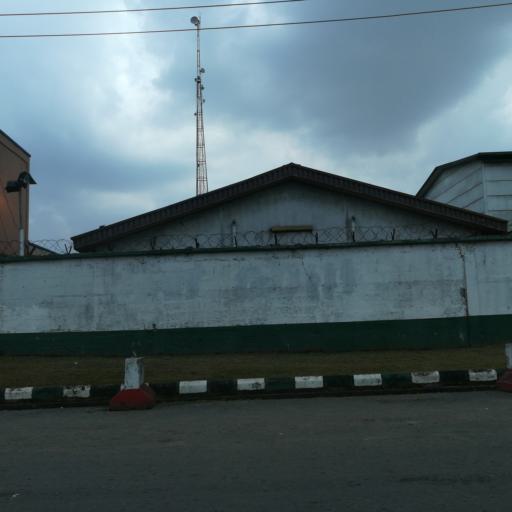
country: NG
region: Rivers
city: Port Harcourt
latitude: 4.8125
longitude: 7.0372
